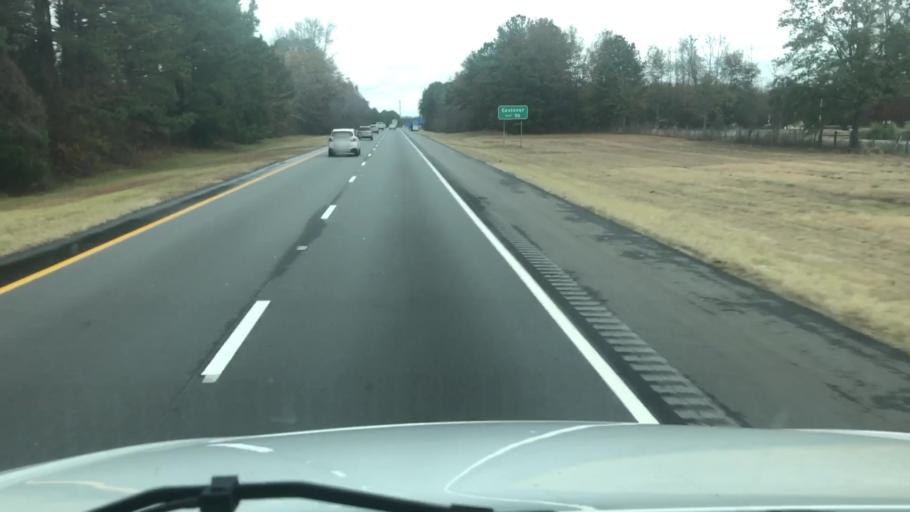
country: US
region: North Carolina
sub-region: Cumberland County
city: Eastover
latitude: 35.0665
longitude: -78.7926
